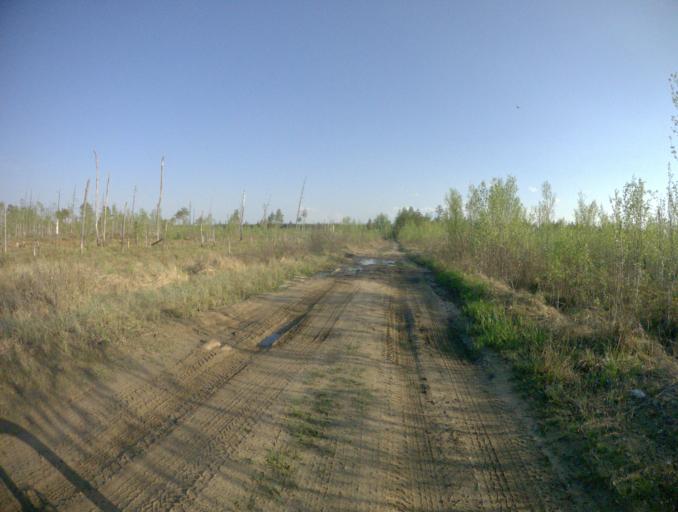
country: RU
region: Vladimir
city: Vyazniki
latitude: 56.3827
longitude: 42.1727
